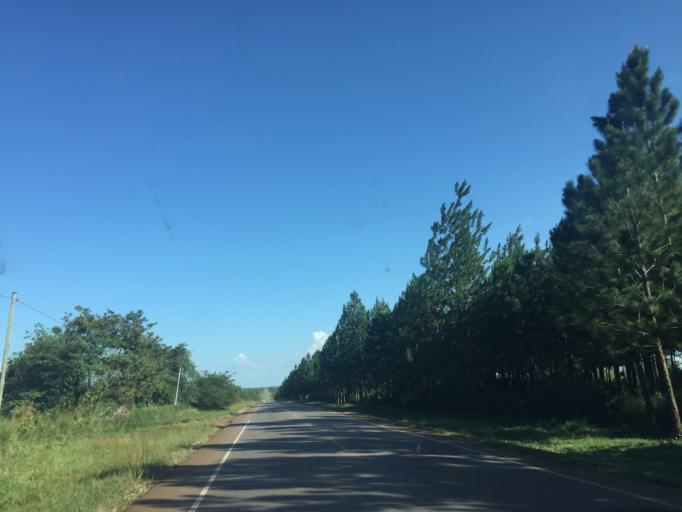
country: UG
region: Central Region
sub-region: Nakasongola District
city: Nakasongola
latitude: 1.3755
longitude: 32.3462
